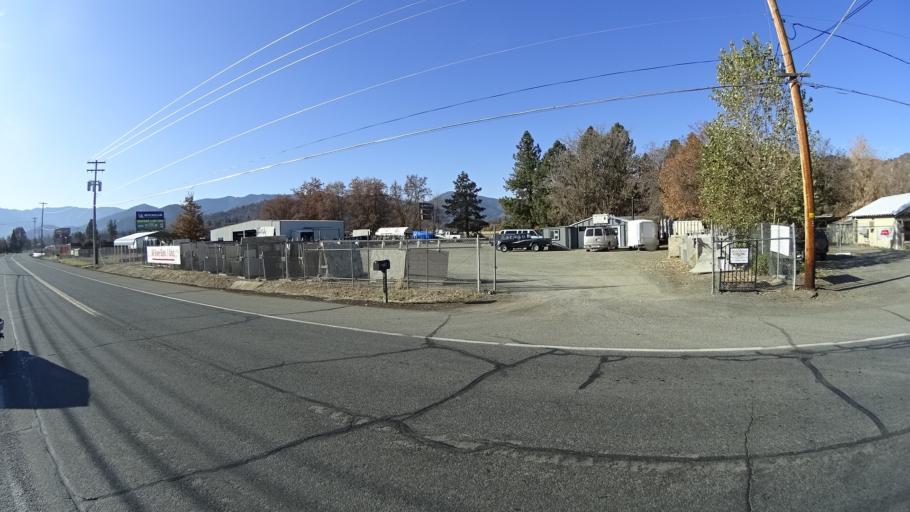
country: US
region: California
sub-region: Siskiyou County
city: Yreka
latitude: 41.6993
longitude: -122.6397
